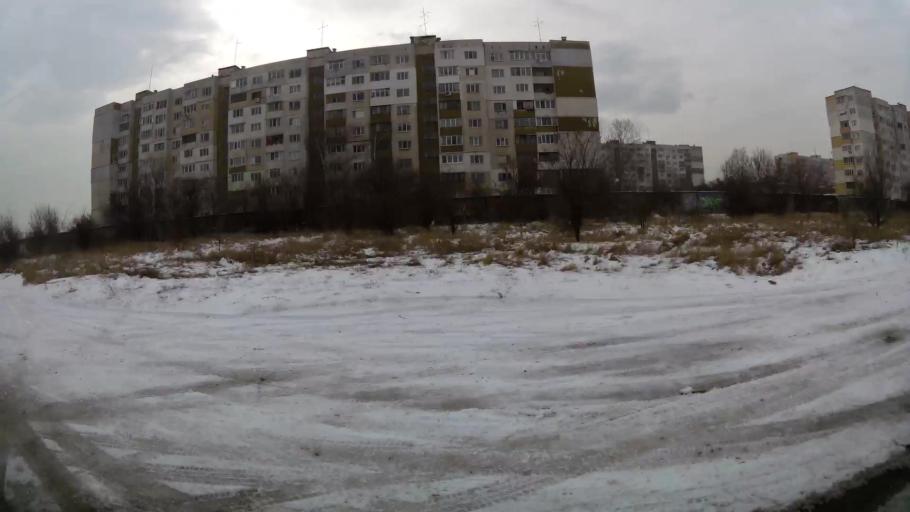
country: BG
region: Sofia-Capital
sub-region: Stolichna Obshtina
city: Sofia
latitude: 42.7145
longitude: 23.3878
